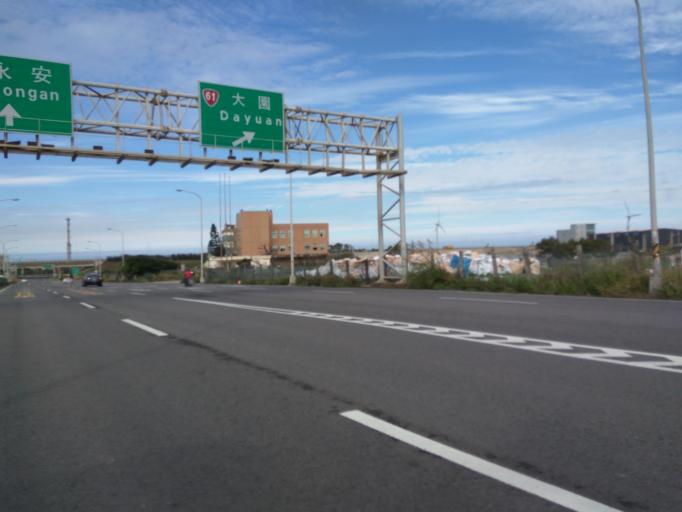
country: TW
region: Taiwan
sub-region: Hsinchu
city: Zhubei
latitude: 25.0280
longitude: 121.0564
